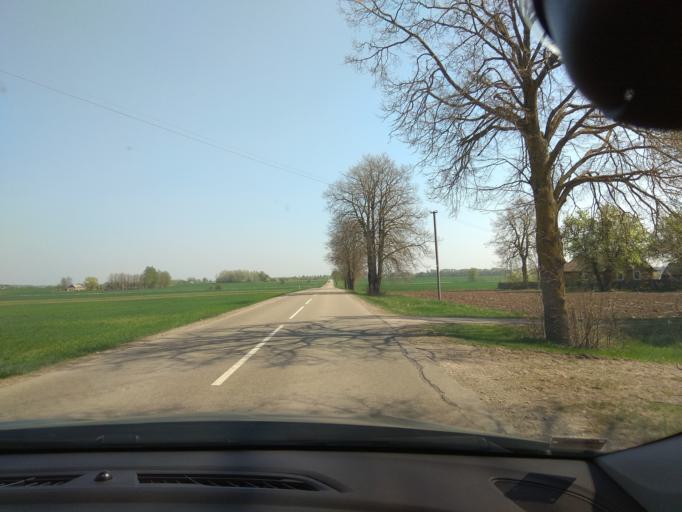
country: LT
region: Panevezys
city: Pasvalys
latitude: 55.9430
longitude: 24.2163
